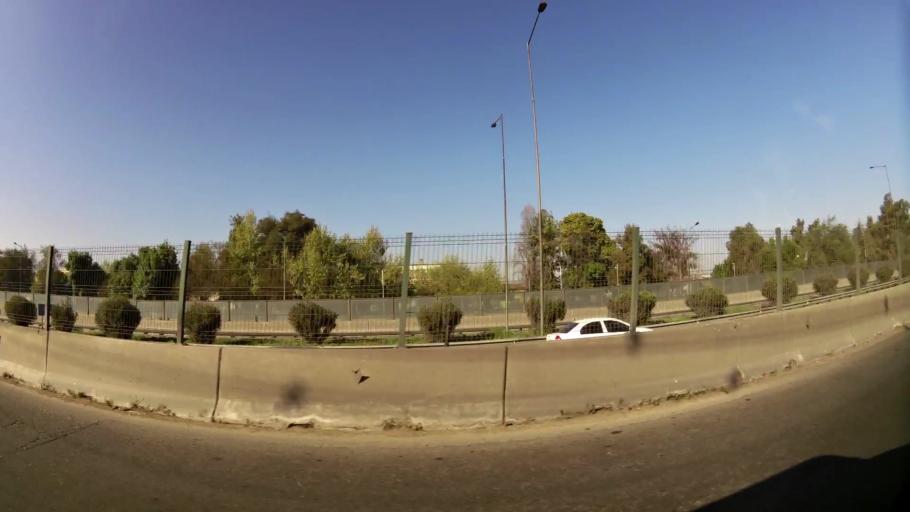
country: CL
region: Santiago Metropolitan
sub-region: Provincia de Santiago
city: Santiago
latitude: -33.3753
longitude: -70.6591
